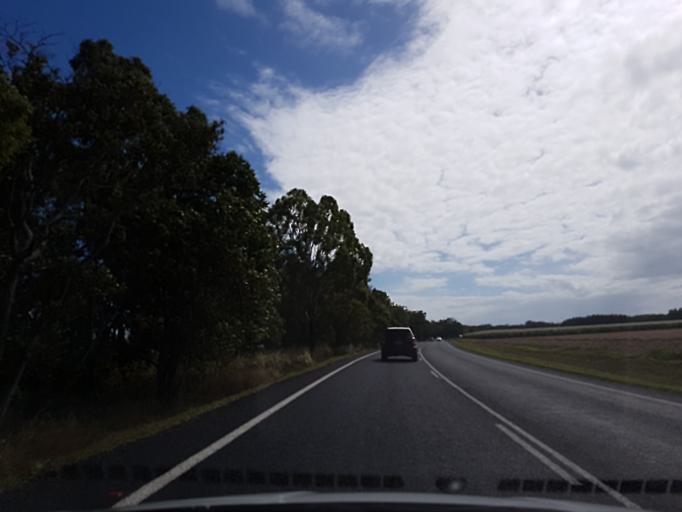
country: AU
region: Queensland
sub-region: Cairns
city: Port Douglas
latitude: -16.5469
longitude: 145.4718
